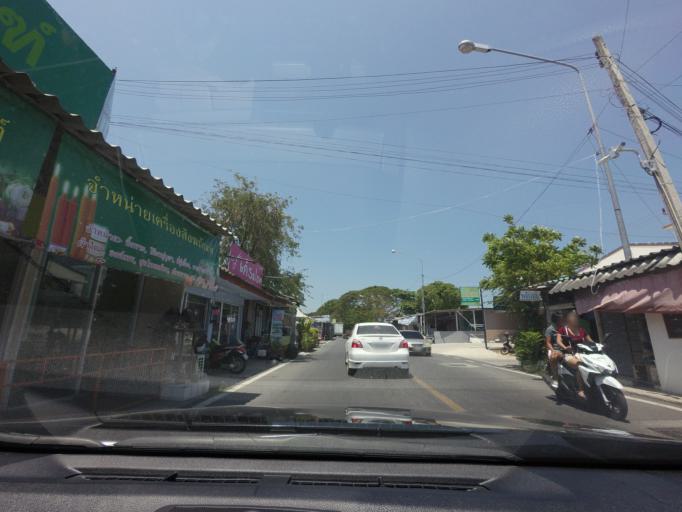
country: TH
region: Prachuap Khiri Khan
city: Hua Hin
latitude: 12.5647
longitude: 99.9554
